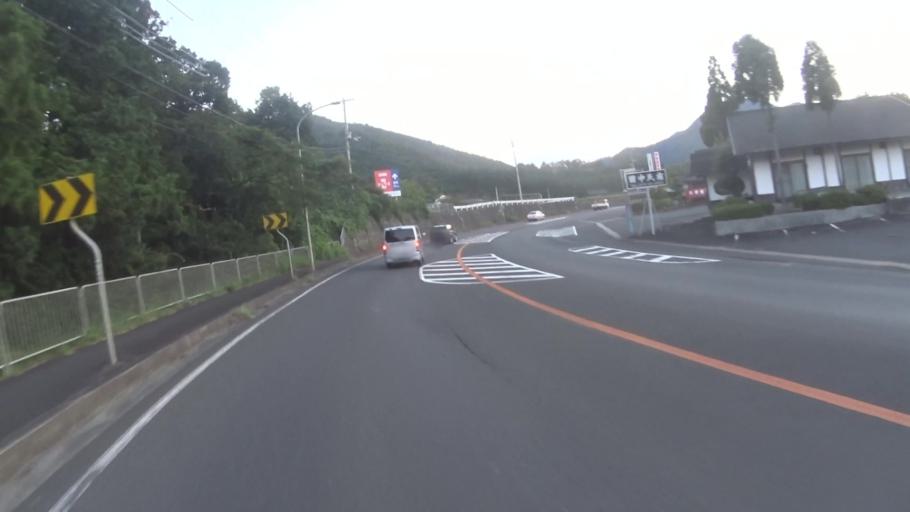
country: JP
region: Kyoto
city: Ayabe
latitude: 35.2589
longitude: 135.4109
